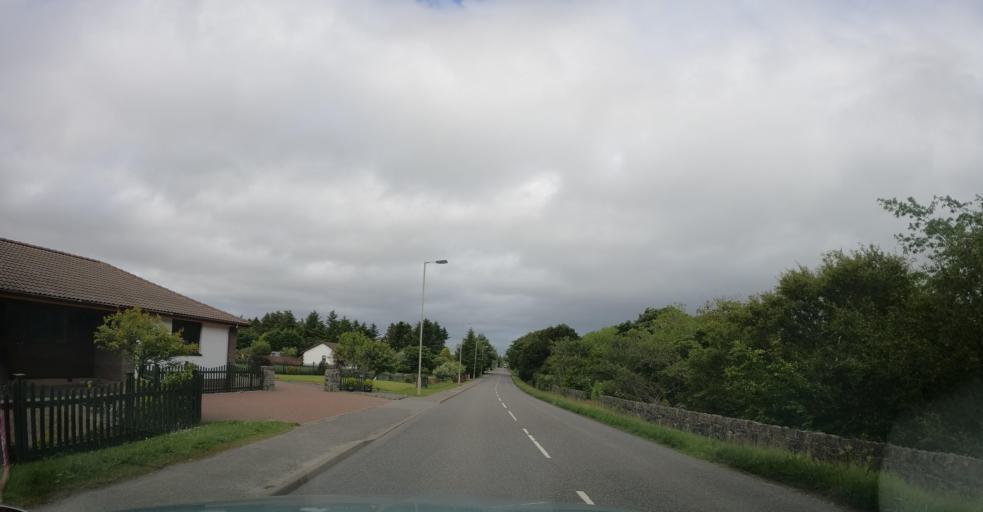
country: GB
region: Scotland
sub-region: Eilean Siar
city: Isle of Lewis
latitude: 58.2157
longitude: -6.4115
